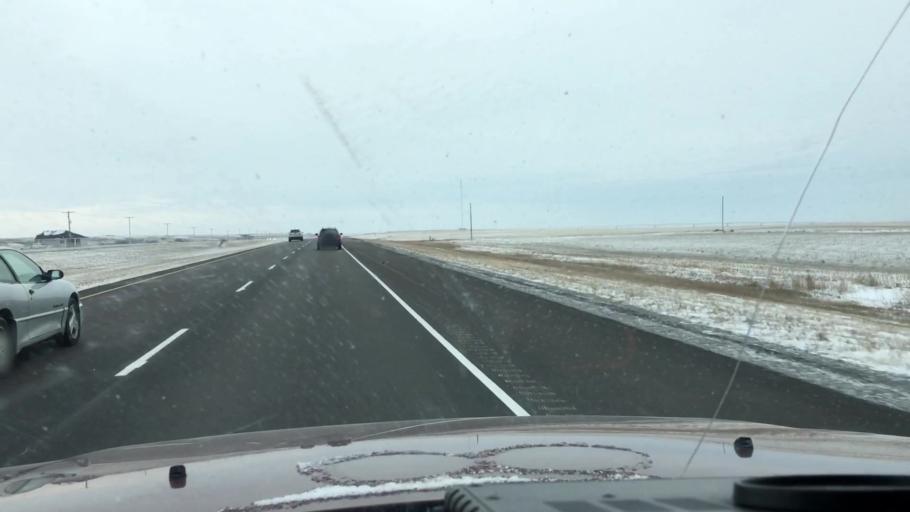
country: CA
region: Saskatchewan
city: Saskatoon
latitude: 51.7528
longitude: -106.4764
